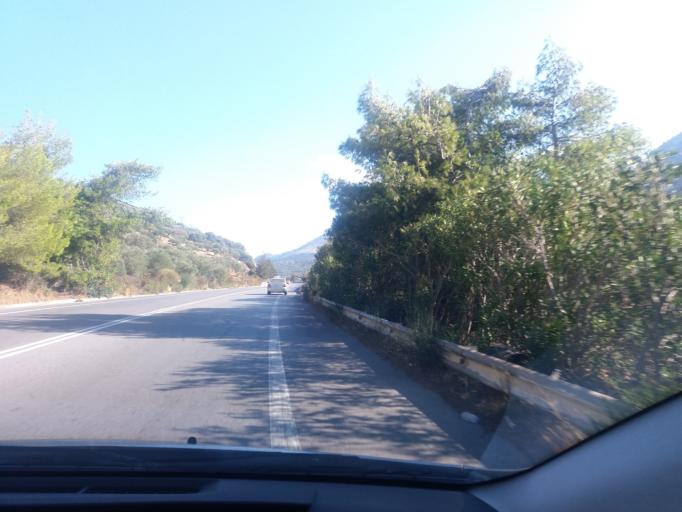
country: GR
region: Crete
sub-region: Nomos Lasithiou
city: Sision
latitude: 35.2822
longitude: 25.5470
